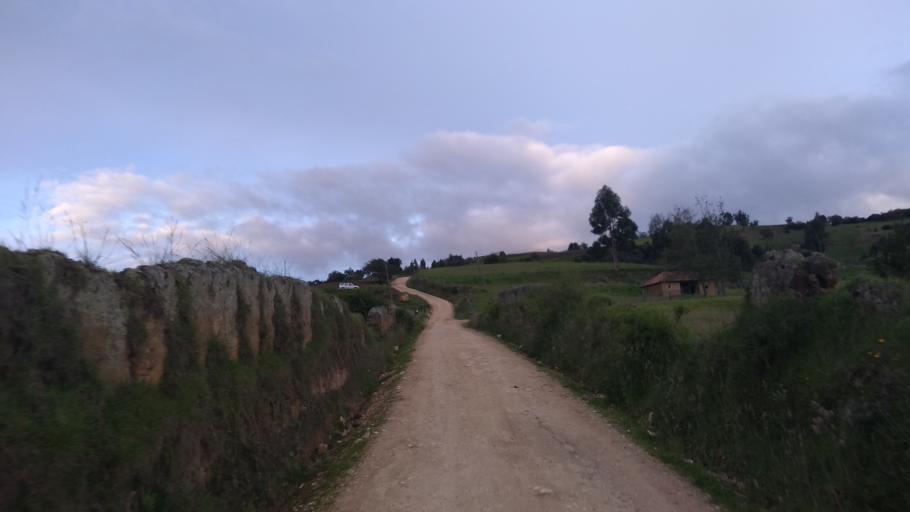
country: CO
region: Boyaca
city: Toca
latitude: 5.5614
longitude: -73.1736
